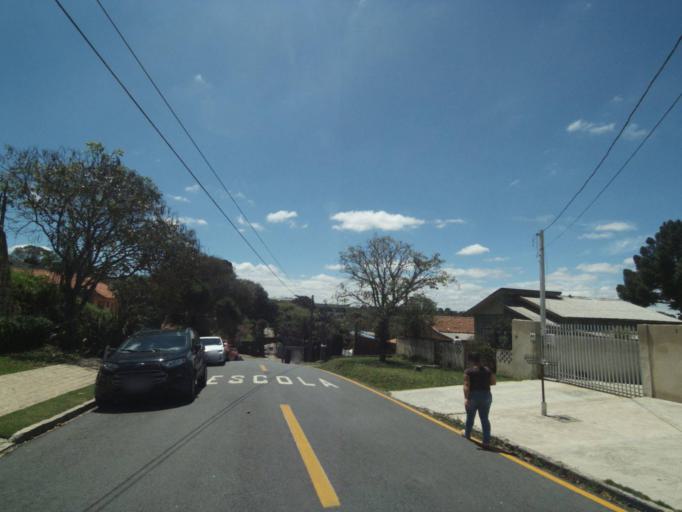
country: BR
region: Parana
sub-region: Curitiba
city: Curitiba
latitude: -25.3906
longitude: -49.2692
